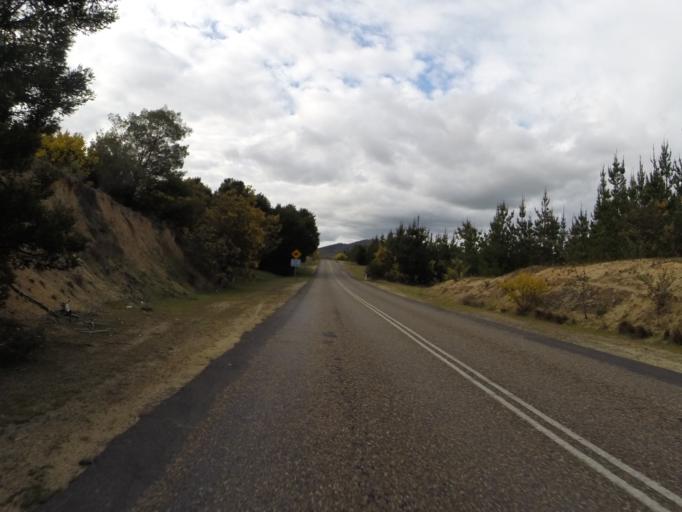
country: AU
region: Australian Capital Territory
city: Macquarie
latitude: -35.3369
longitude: 148.9301
